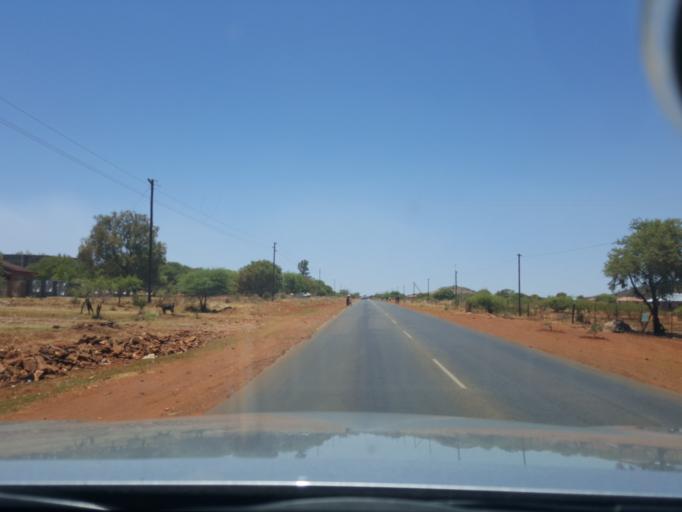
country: ZA
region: North-West
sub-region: Ngaka Modiri Molema District Municipality
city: Zeerust
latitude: -25.4622
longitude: 25.9716
